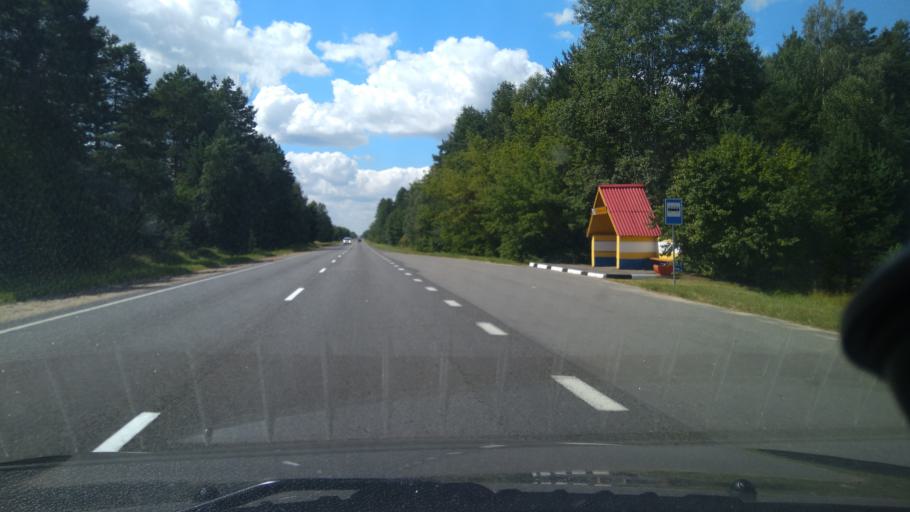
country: BY
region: Brest
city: Nyakhachava
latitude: 52.6575
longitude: 25.2328
